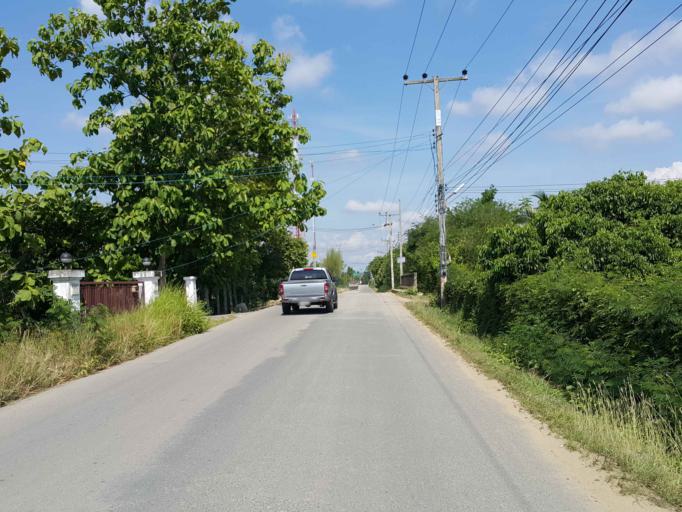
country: TH
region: Chiang Mai
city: Saraphi
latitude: 18.7206
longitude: 99.0766
